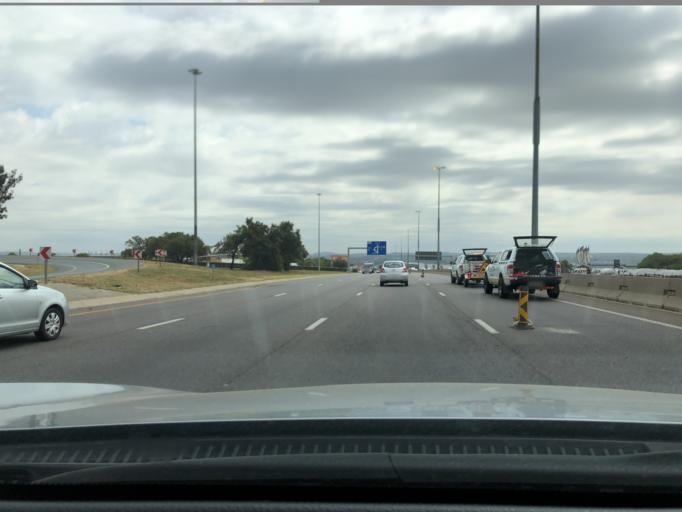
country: ZA
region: Gauteng
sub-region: City of Tshwane Metropolitan Municipality
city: Centurion
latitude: -25.9056
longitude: 28.1595
